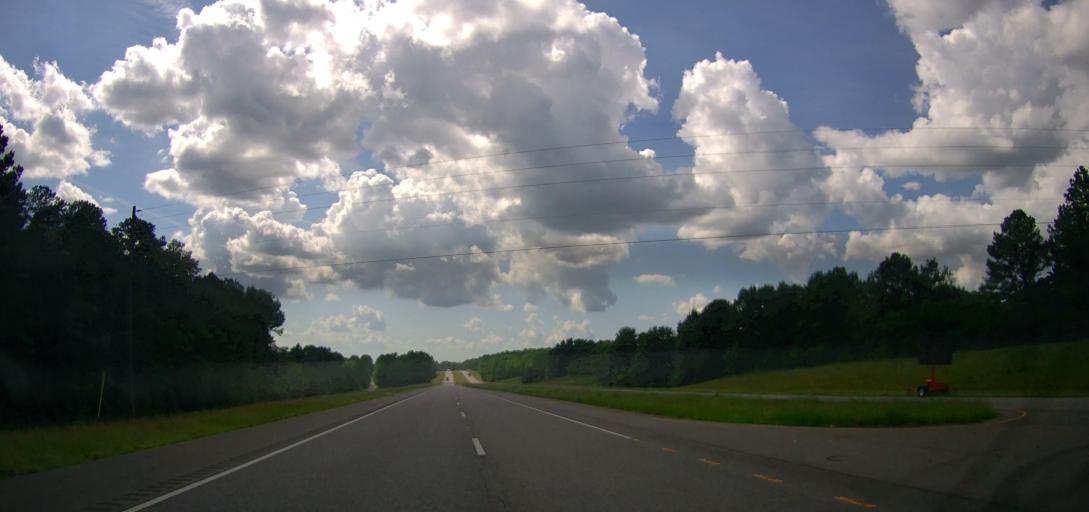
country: US
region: Alabama
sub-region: Pickens County
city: Reform
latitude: 33.3986
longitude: -88.0624
